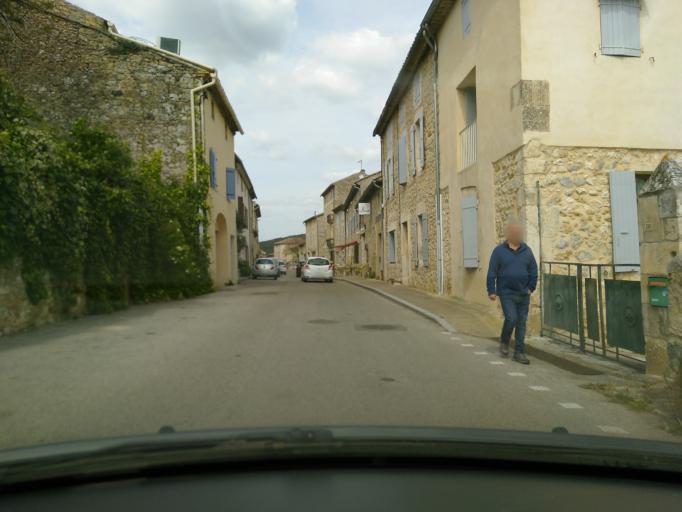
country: FR
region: Rhone-Alpes
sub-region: Departement de l'Ardeche
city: Ruoms
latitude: 44.4464
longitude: 4.4168
